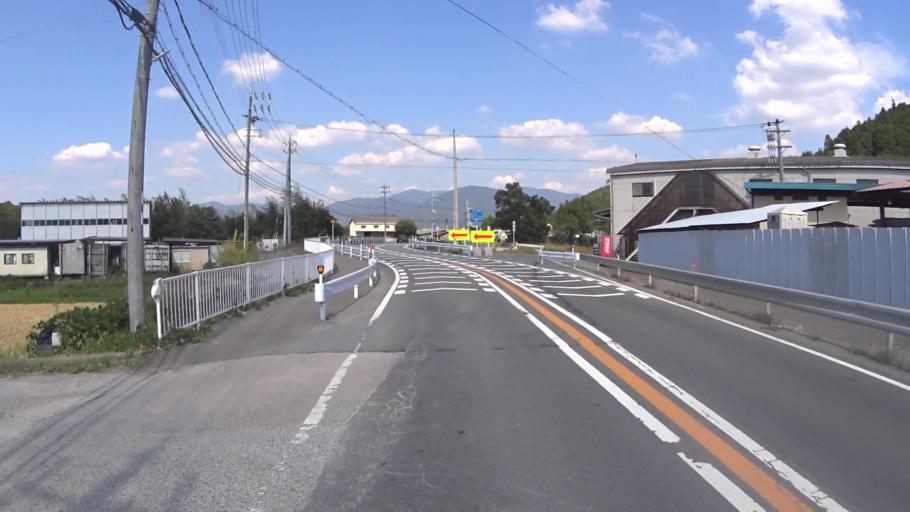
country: JP
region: Kyoto
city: Kameoka
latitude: 35.0059
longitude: 135.5576
